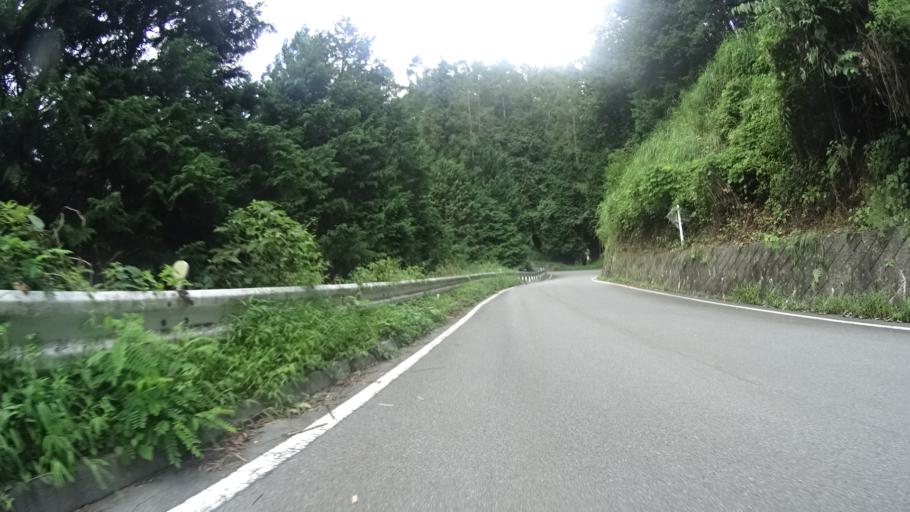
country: JP
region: Yamanashi
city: Enzan
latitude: 35.7909
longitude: 138.6843
